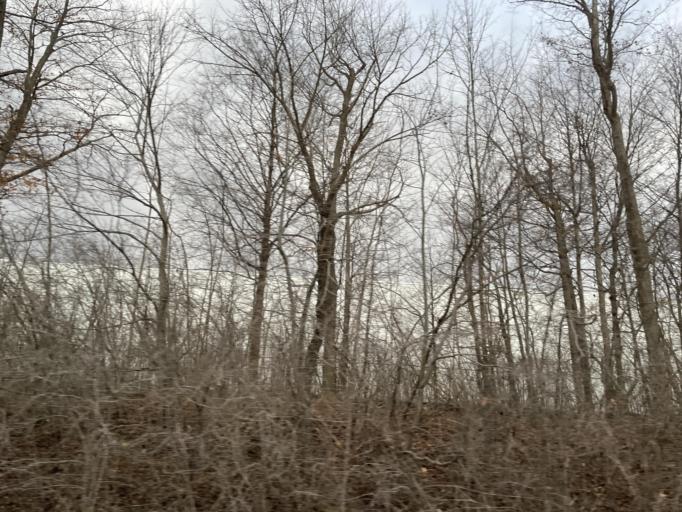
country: CA
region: Ontario
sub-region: Wellington County
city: Guelph
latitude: 43.5384
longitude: -80.2988
